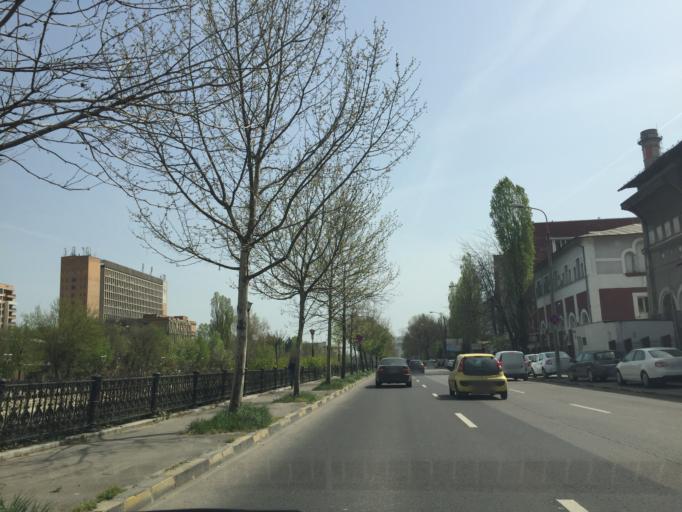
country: RO
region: Bucuresti
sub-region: Municipiul Bucuresti
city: Bucuresti
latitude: 44.4420
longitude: 26.0632
